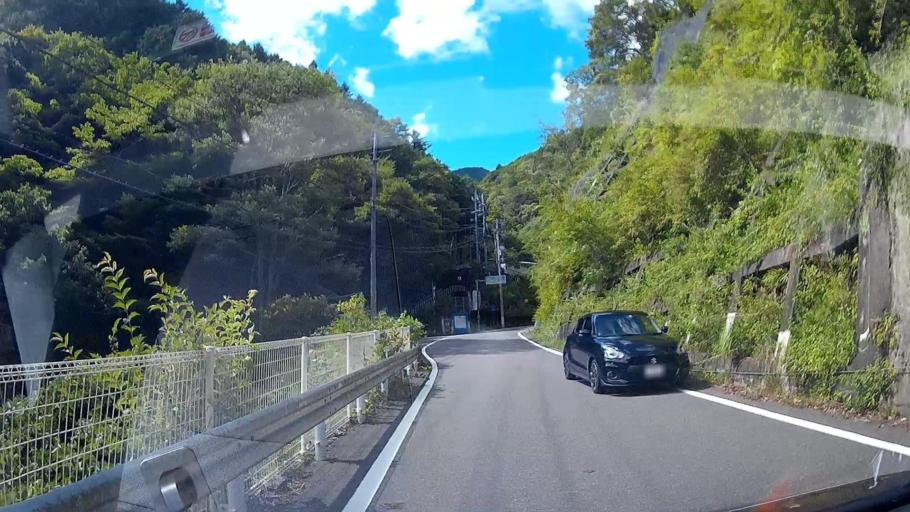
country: JP
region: Shizuoka
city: Shizuoka-shi
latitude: 35.2115
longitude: 138.2216
